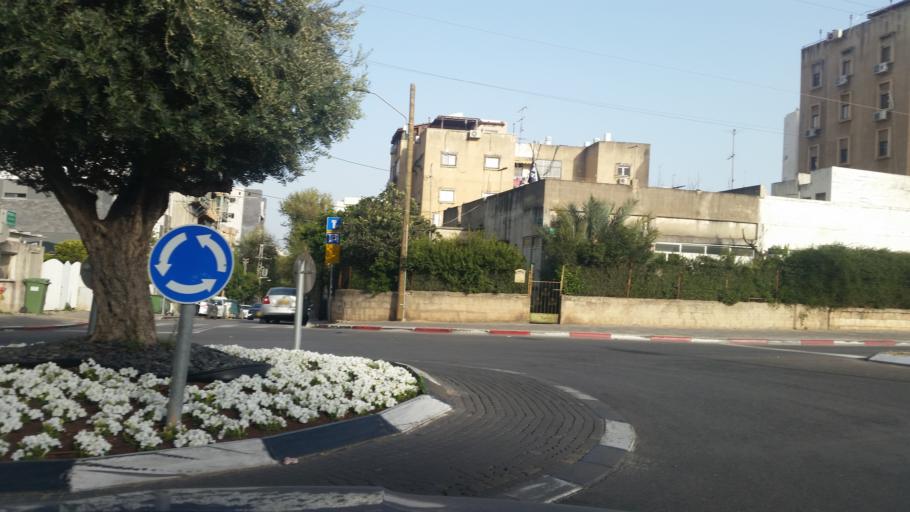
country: IL
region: Tel Aviv
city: Bene Beraq
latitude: 32.0708
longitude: 34.8326
